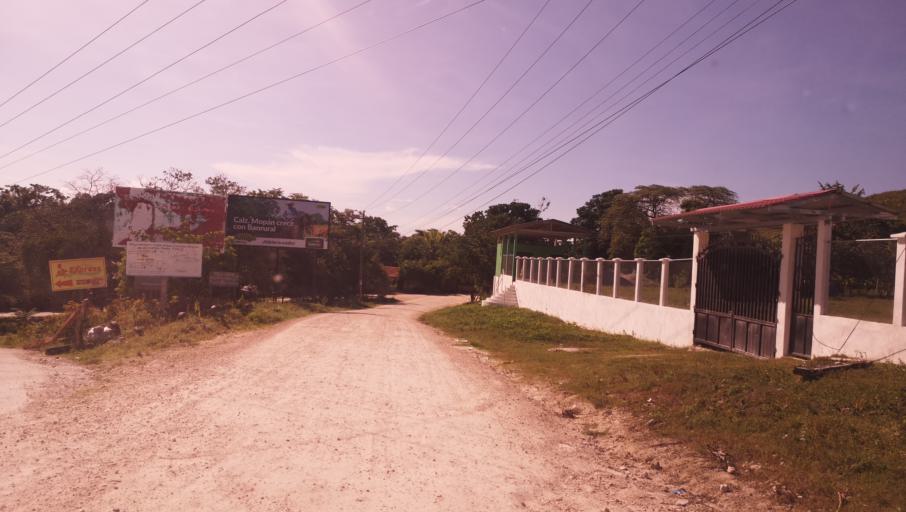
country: GT
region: Peten
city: Dolores
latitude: 16.7262
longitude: -89.3804
